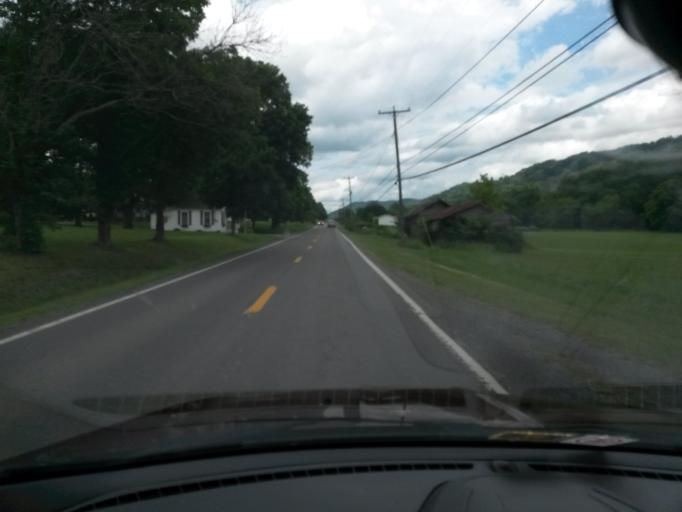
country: US
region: Virginia
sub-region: Giles County
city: Pearisburg
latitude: 37.4375
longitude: -80.6973
